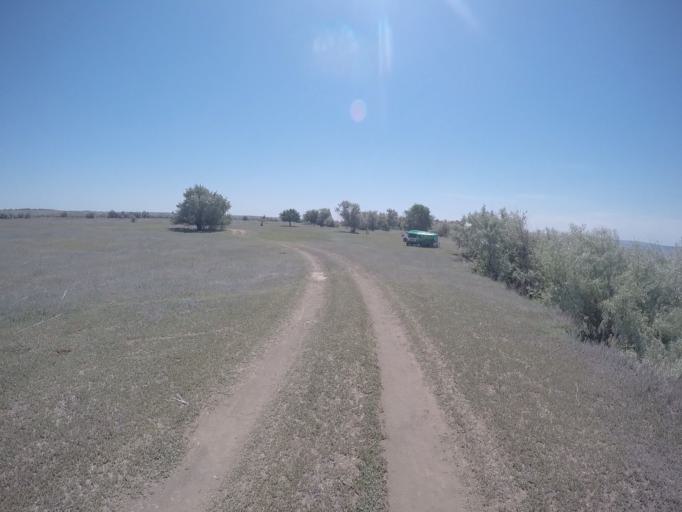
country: RU
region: Saratov
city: Krasnoarmeysk
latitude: 51.1666
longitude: 45.9037
